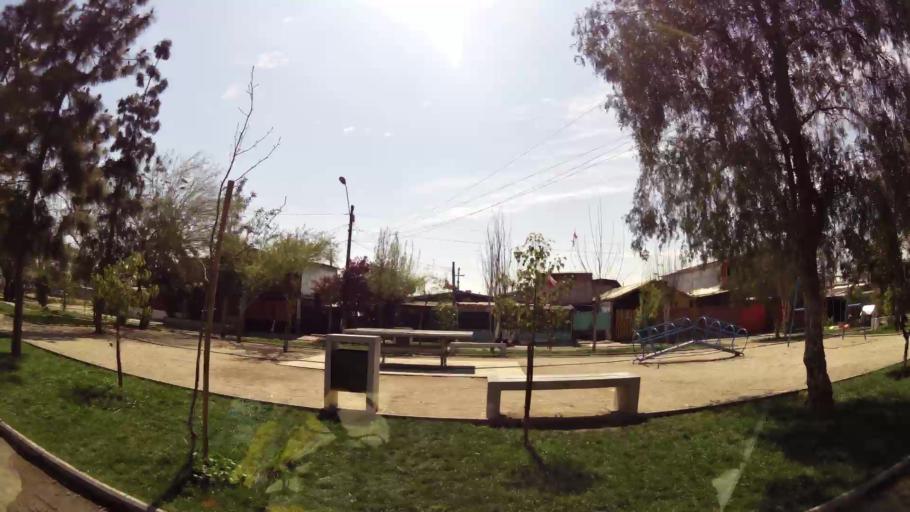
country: CL
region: Santiago Metropolitan
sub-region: Provincia de Santiago
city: La Pintana
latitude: -33.5440
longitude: -70.6506
